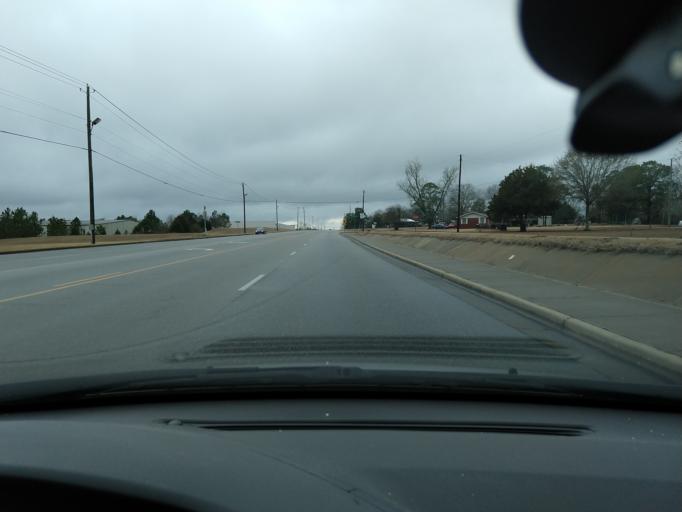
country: US
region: Alabama
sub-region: Houston County
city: Dothan
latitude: 31.2716
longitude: -85.3961
